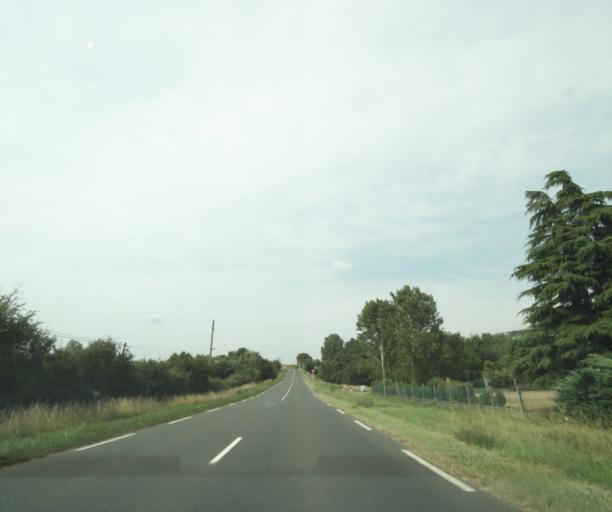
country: FR
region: Centre
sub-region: Departement d'Indre-et-Loire
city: Neuille-Pont-Pierre
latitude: 47.5607
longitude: 0.5496
